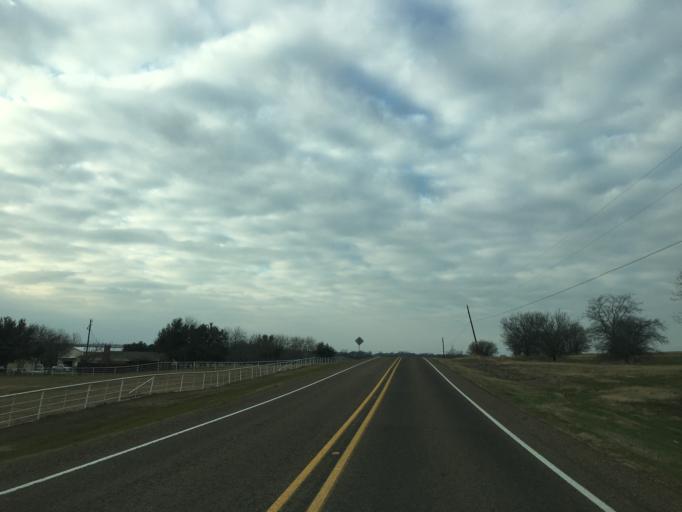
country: US
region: Texas
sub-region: Ellis County
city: Palmer
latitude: 32.4341
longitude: -96.6862
